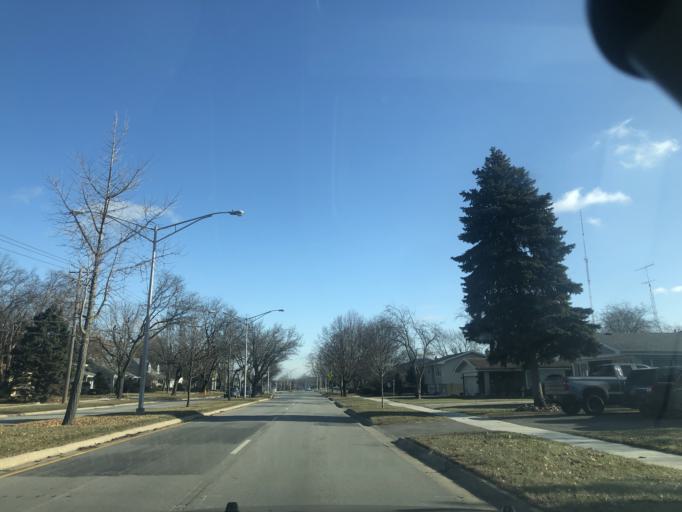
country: US
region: Illinois
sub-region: DuPage County
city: Addison
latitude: 41.9294
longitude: -88.0129
